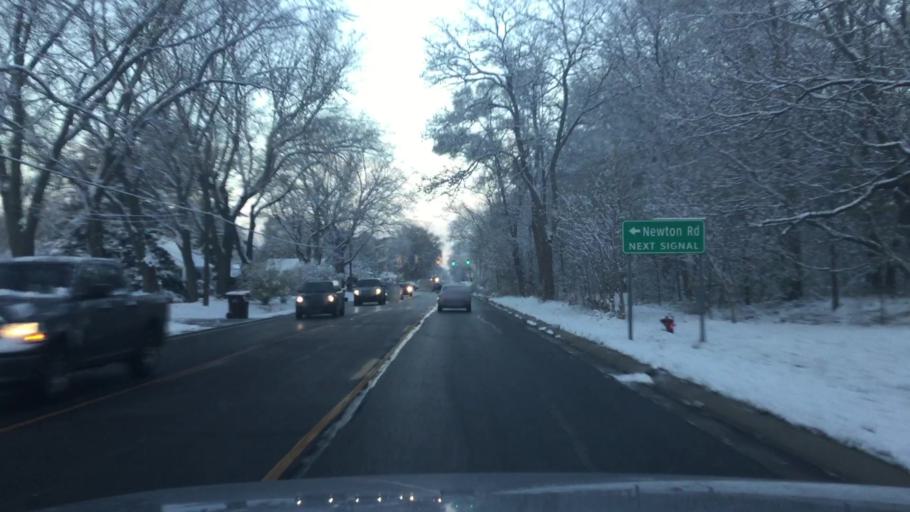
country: US
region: Michigan
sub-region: Oakland County
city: Wolverine Lake
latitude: 42.5917
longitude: -83.4690
